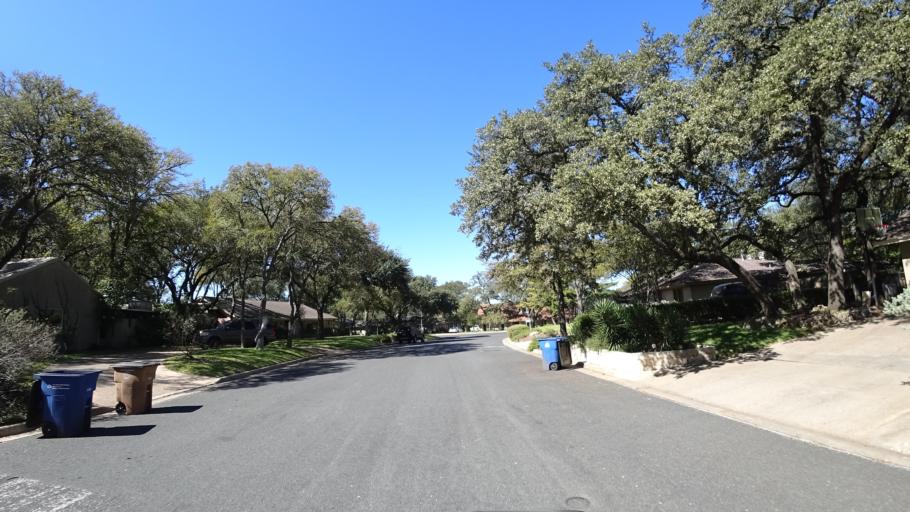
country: US
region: Texas
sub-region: Travis County
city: West Lake Hills
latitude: 30.3637
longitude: -97.7695
